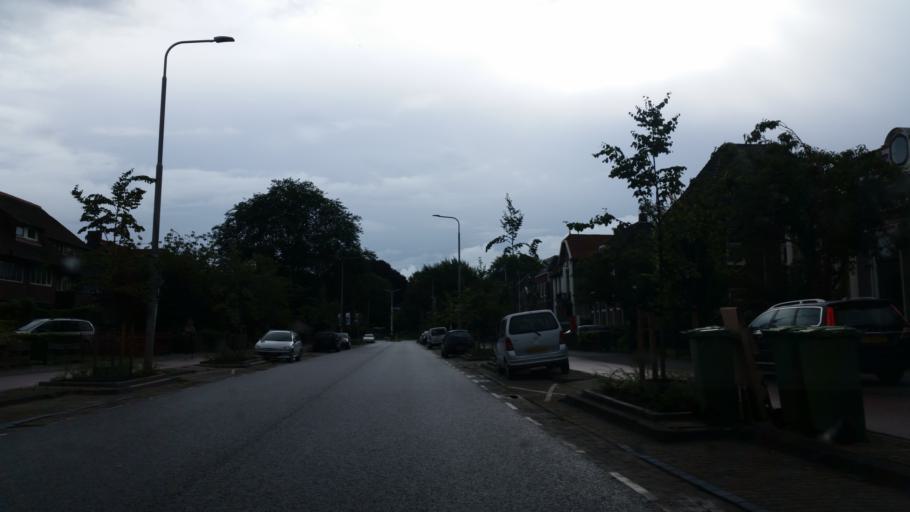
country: NL
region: Friesland
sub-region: Gemeente Leeuwarden
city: Bilgaard
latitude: 53.2042
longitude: 5.7848
